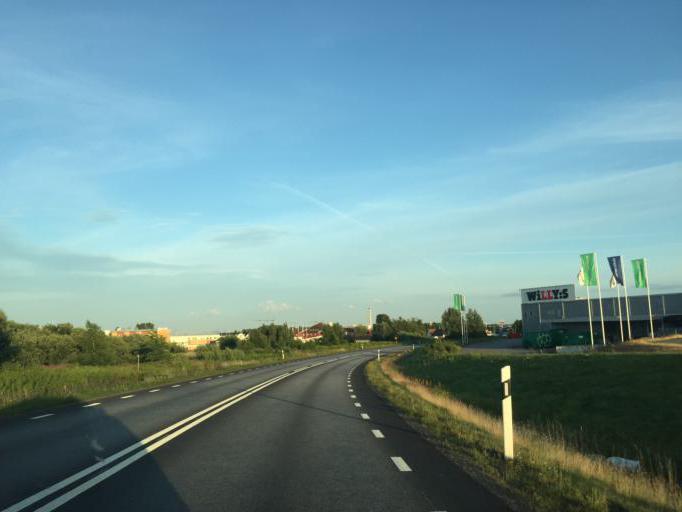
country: SE
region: Skane
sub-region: Angelholms Kommun
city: AEngelholm
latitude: 56.2573
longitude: 12.8911
